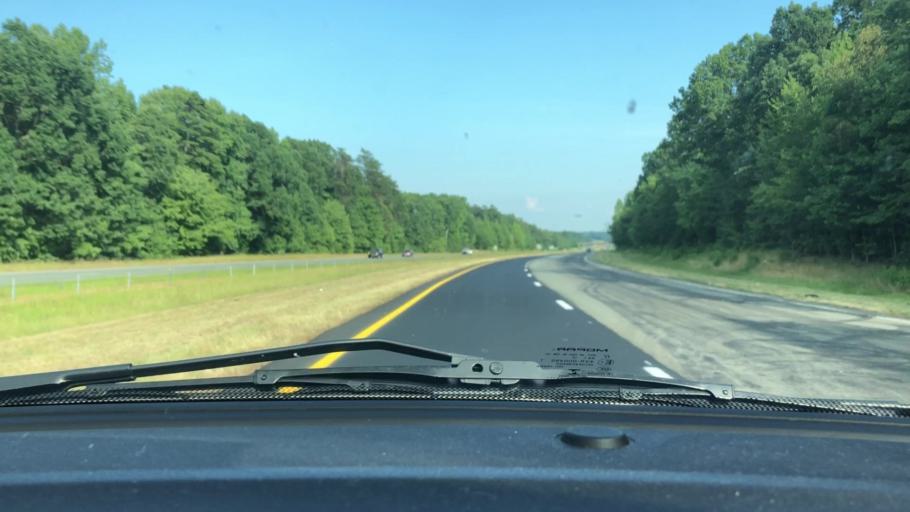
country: US
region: North Carolina
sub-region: Randolph County
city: Liberty
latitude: 35.8113
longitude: -79.5496
